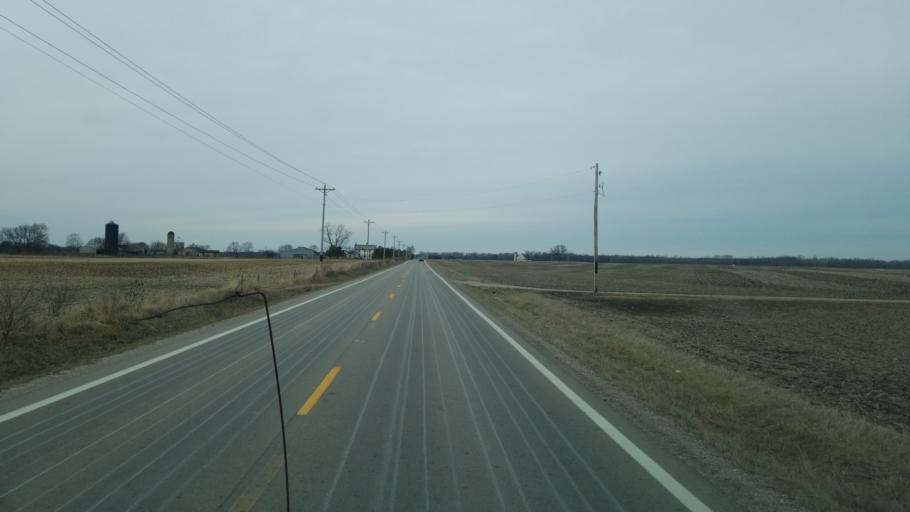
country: US
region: Ohio
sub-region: Pickaway County
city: Circleville
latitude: 39.6039
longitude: -83.0045
